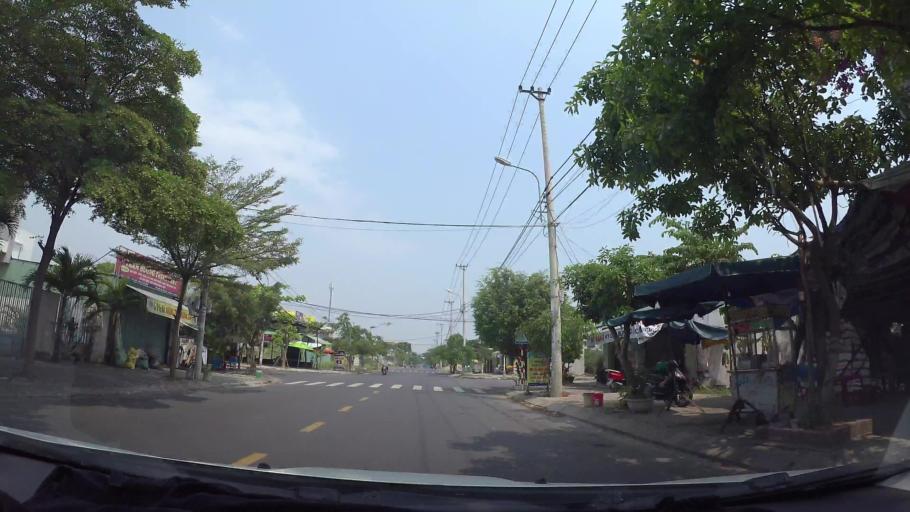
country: VN
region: Da Nang
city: Cam Le
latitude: 15.9939
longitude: 108.2135
